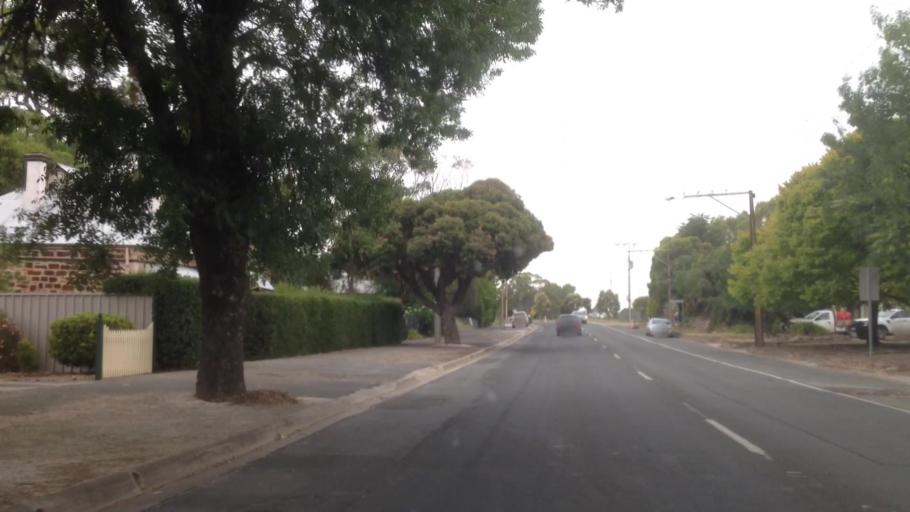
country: AU
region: South Australia
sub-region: Barossa
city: Lyndoch
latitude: -34.6035
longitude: 138.8913
